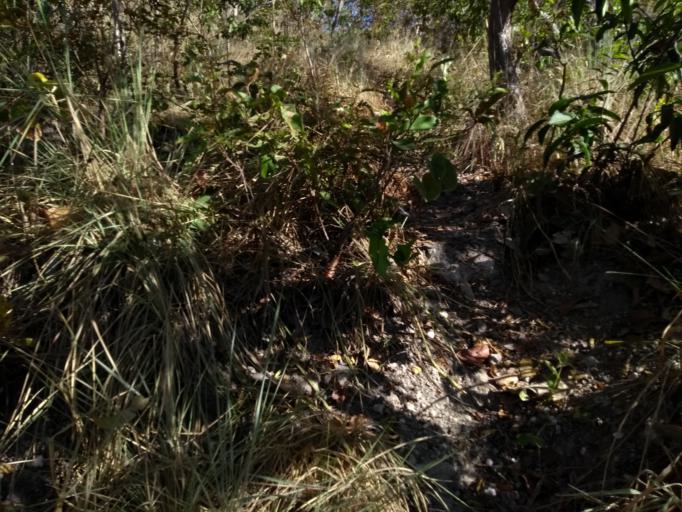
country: BR
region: Goias
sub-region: Cavalcante
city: Cavalcante
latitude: -13.8004
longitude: -47.4494
